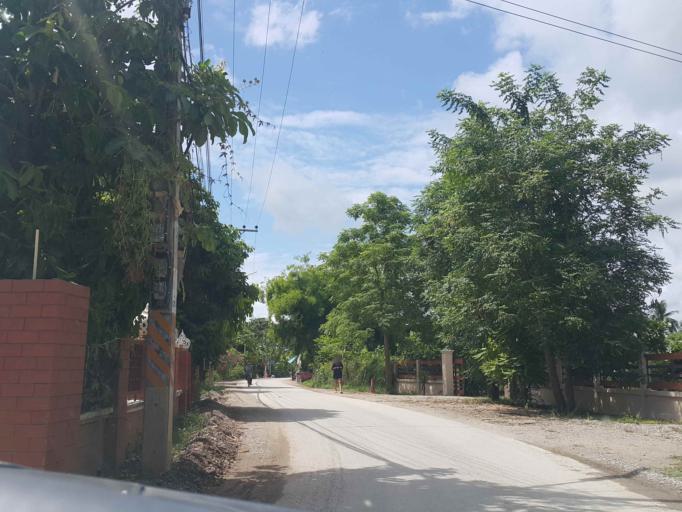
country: TH
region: Chiang Mai
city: Saraphi
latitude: 18.7314
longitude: 99.0497
